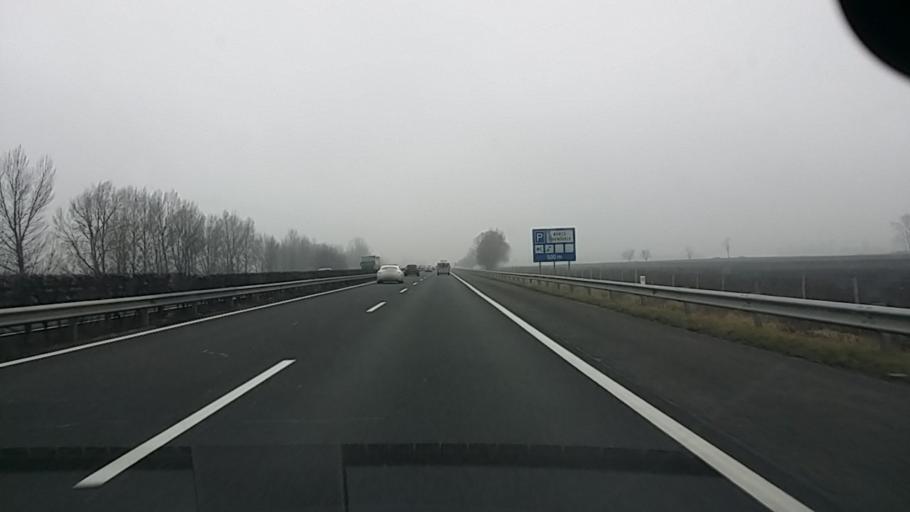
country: HU
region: Gyor-Moson-Sopron
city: Otteveny
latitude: 47.7000
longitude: 17.5004
